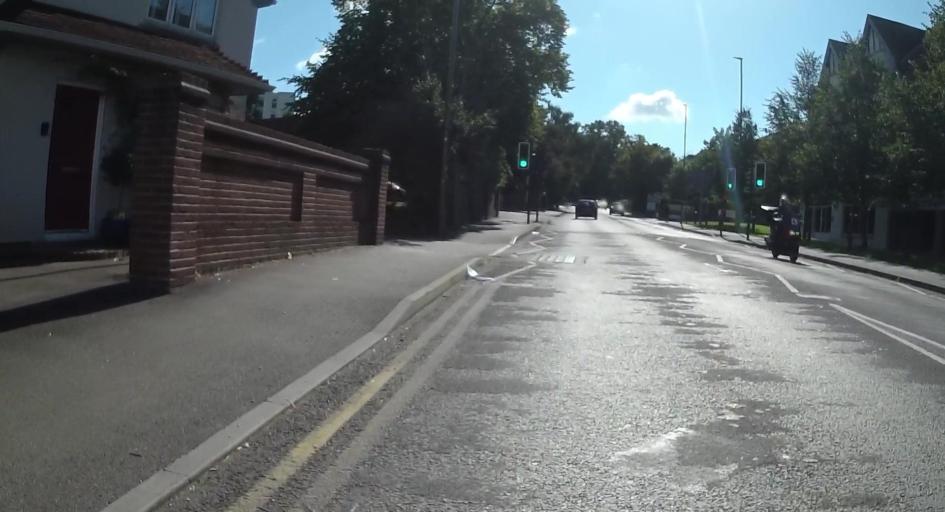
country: GB
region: England
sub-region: Surrey
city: Weybridge
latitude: 51.3731
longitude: -0.4541
